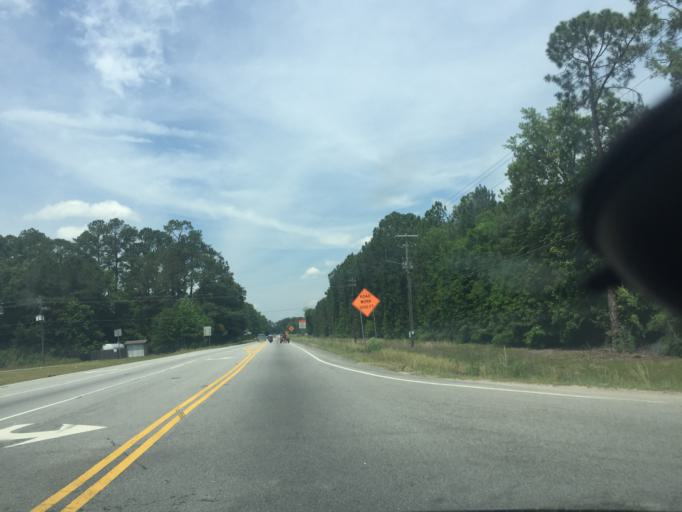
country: US
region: Georgia
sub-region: Chatham County
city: Bloomingdale
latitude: 32.1846
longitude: -81.4002
